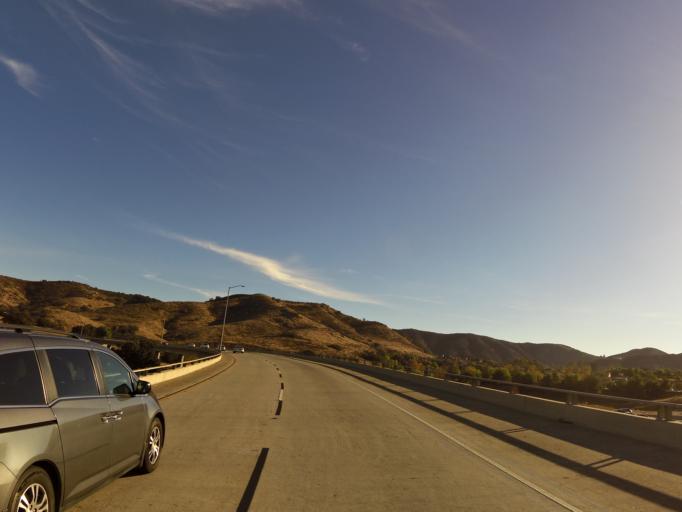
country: US
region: California
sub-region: Ventura County
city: Thousand Oaks
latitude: 34.1774
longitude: -118.8607
